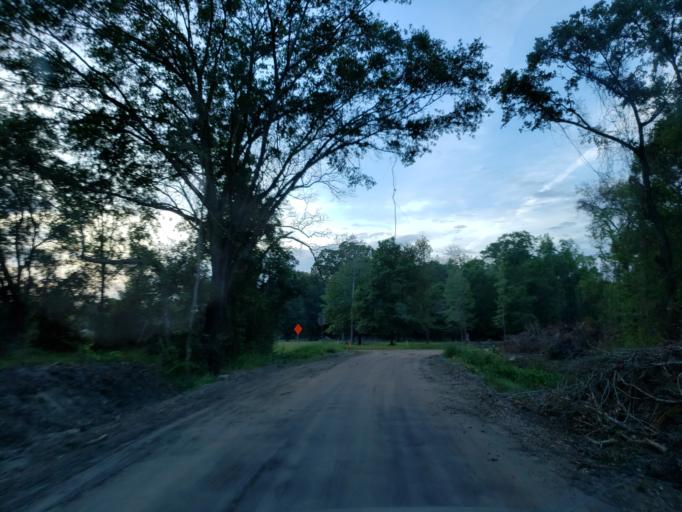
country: US
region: Georgia
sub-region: Lowndes County
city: Hahira
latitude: 30.9559
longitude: -83.3932
